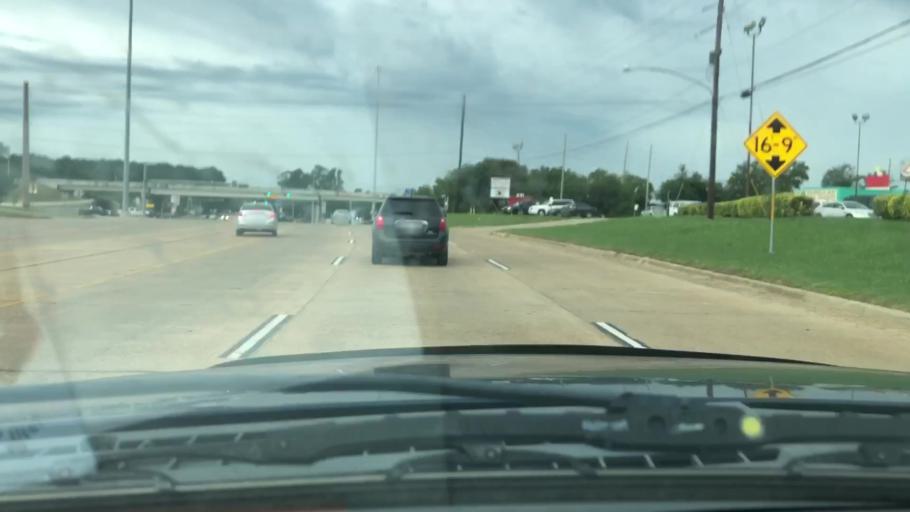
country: US
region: Texas
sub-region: Bowie County
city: Wake Village
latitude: 33.4433
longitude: -94.0945
